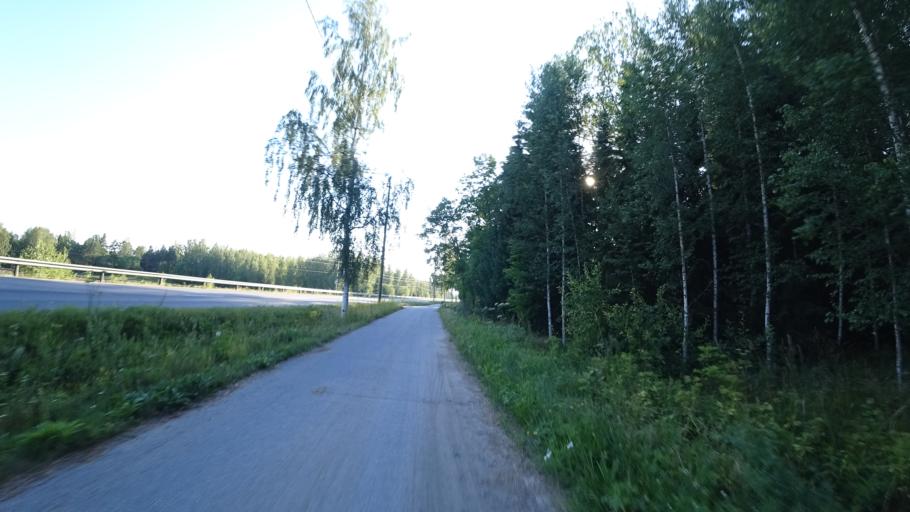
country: FI
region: Pirkanmaa
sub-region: Tampere
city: Nokia
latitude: 61.4676
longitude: 23.4460
